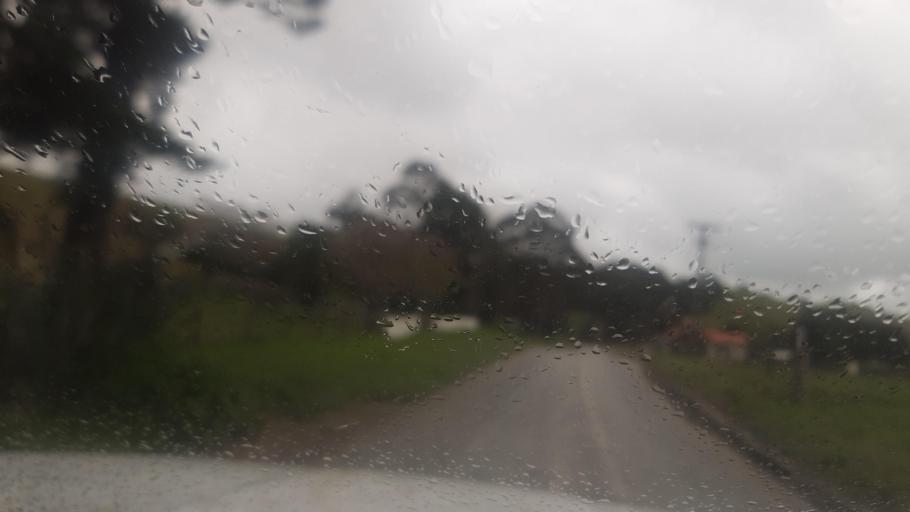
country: NZ
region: Northland
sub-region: Far North District
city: Taipa
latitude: -35.1024
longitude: 173.3994
